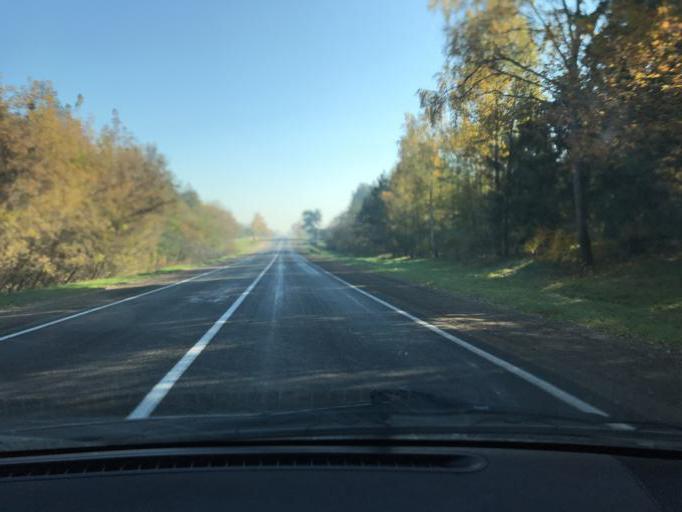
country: BY
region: Brest
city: Lyakhavichy
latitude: 52.9622
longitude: 26.4454
